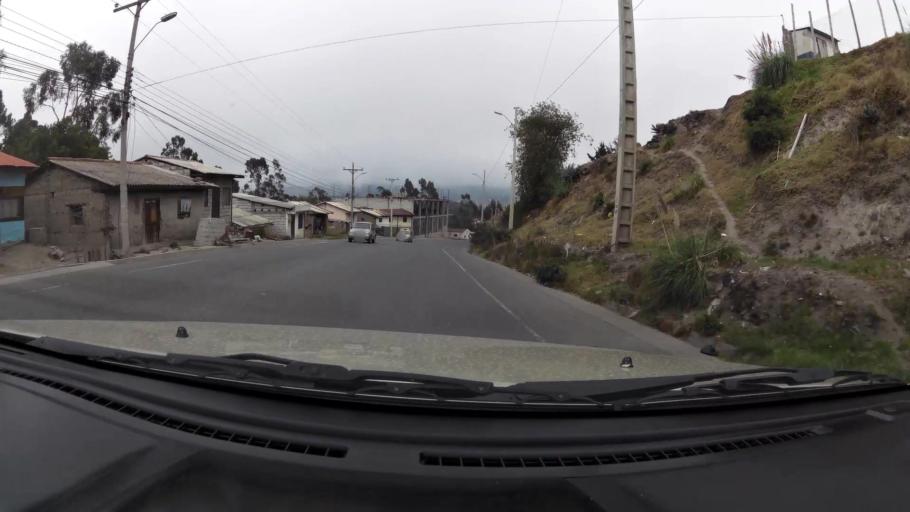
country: EC
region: Canar
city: Canar
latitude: -2.5431
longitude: -78.9408
